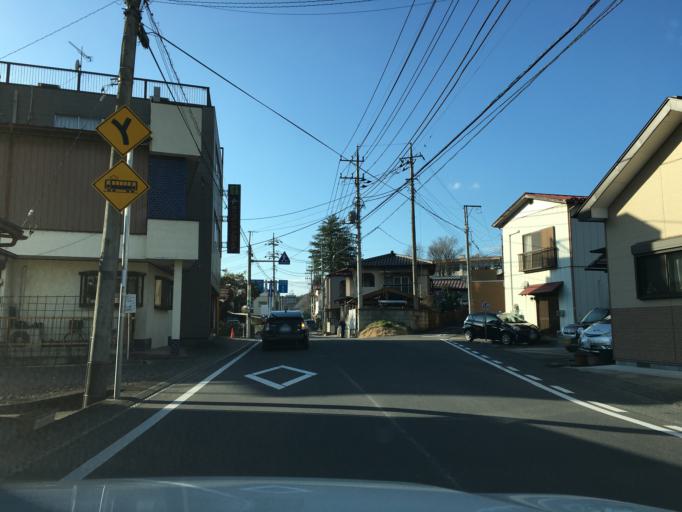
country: JP
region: Ibaraki
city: Daigo
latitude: 36.7753
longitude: 140.3482
